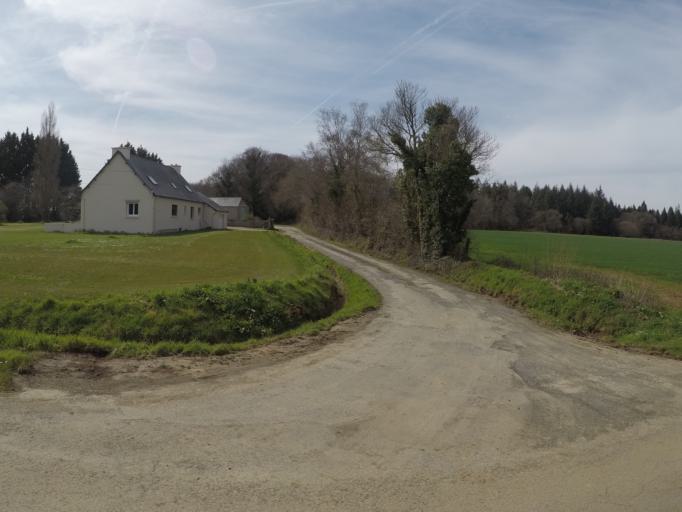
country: FR
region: Brittany
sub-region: Departement des Cotes-d'Armor
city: Plelo
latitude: 48.5822
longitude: -2.9306
